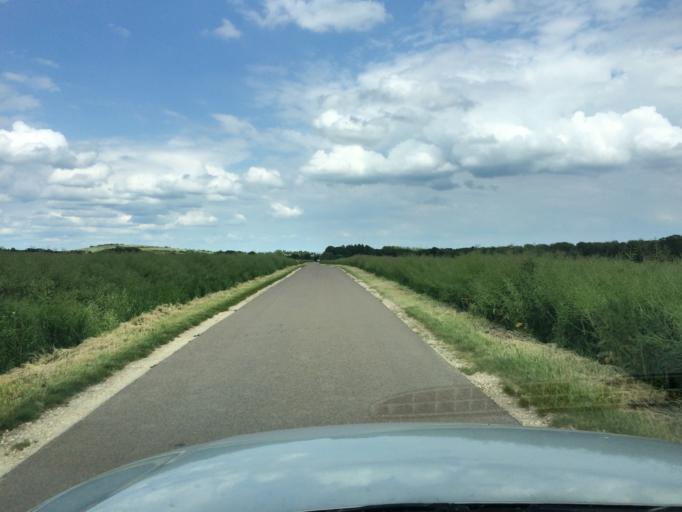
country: FR
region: Bourgogne
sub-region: Departement de l'Yonne
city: Aillant-sur-Tholon
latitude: 47.8733
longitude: 3.3991
